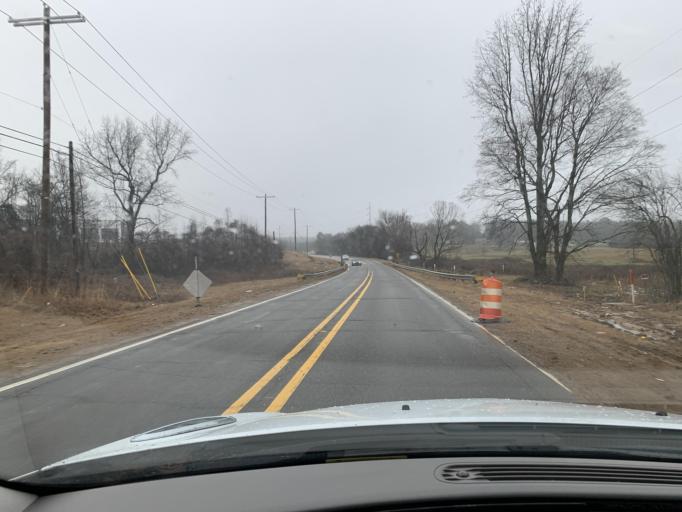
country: US
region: Mississippi
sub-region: De Soto County
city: Horn Lake
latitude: 34.9126
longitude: -90.0027
